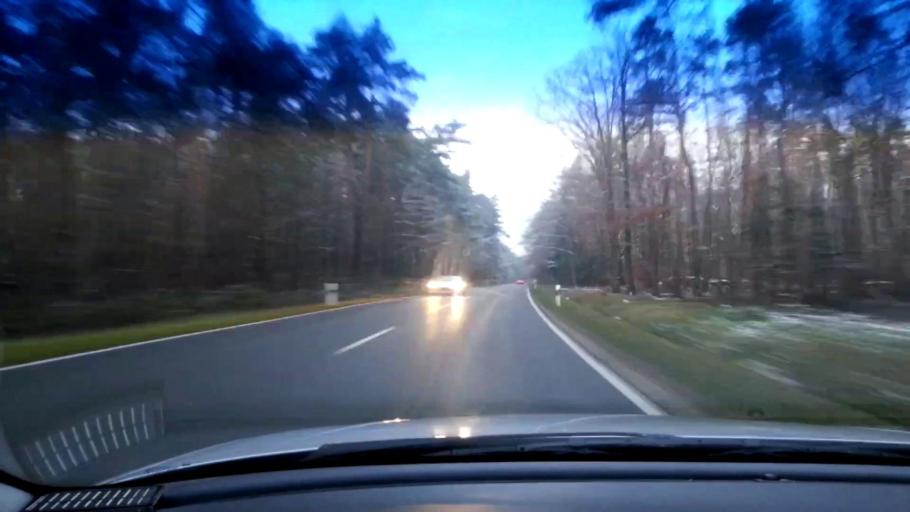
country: DE
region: Bavaria
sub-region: Upper Franconia
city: Pommersfelden
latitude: 49.7985
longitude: 10.8274
